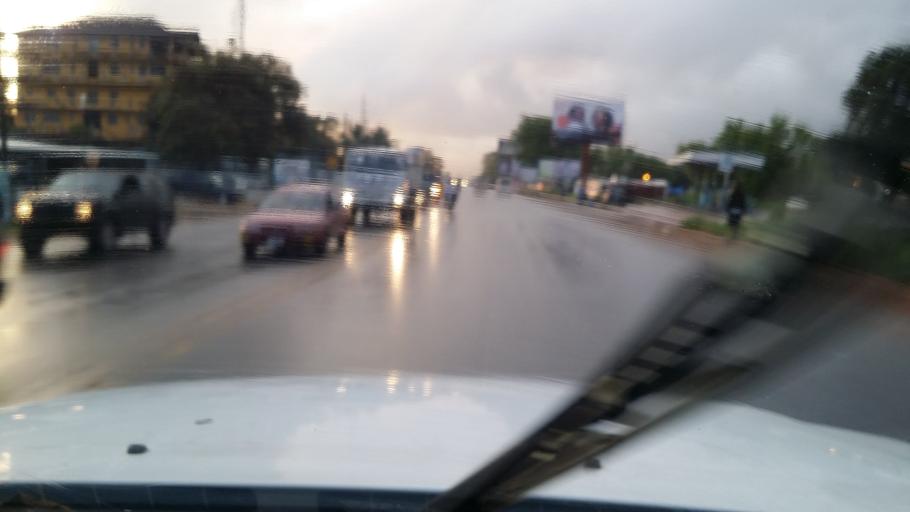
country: LR
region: Montserrado
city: Monrovia
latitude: 6.2796
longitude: -10.7633
